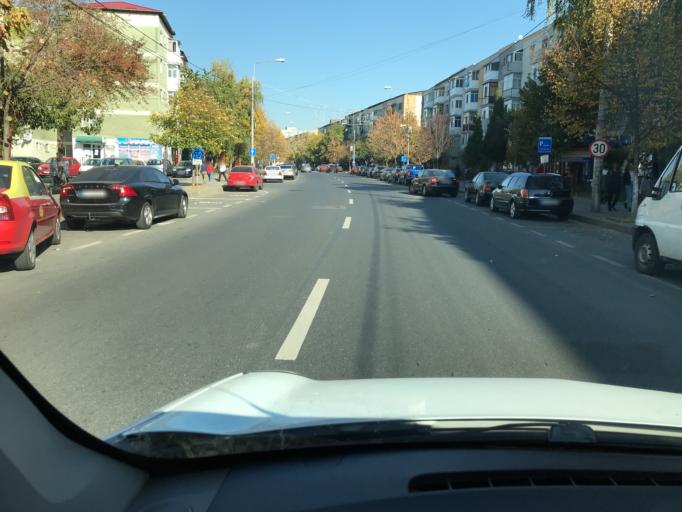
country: RO
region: Olt
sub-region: Municipiul Slatina
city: Slatina
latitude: 44.4285
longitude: 24.3735
